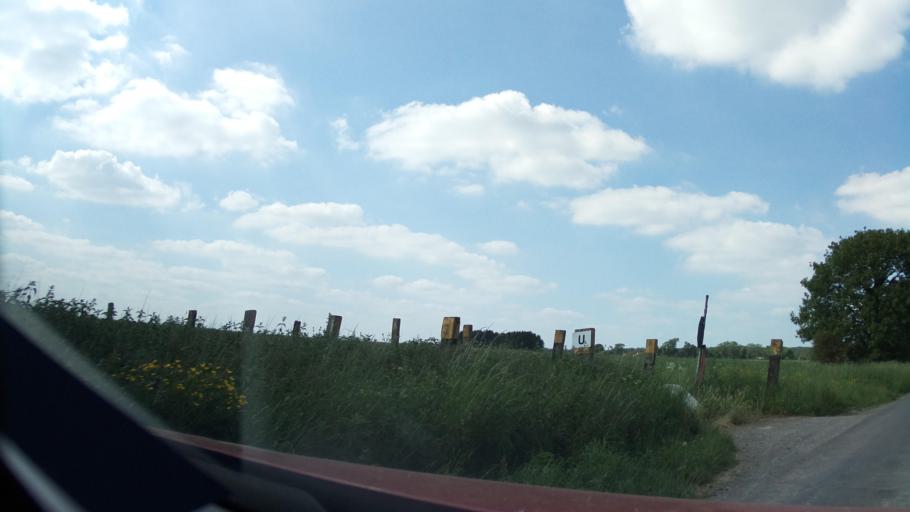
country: GB
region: England
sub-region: Wiltshire
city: Collingbourne Kingston
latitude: 51.2735
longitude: -1.7086
